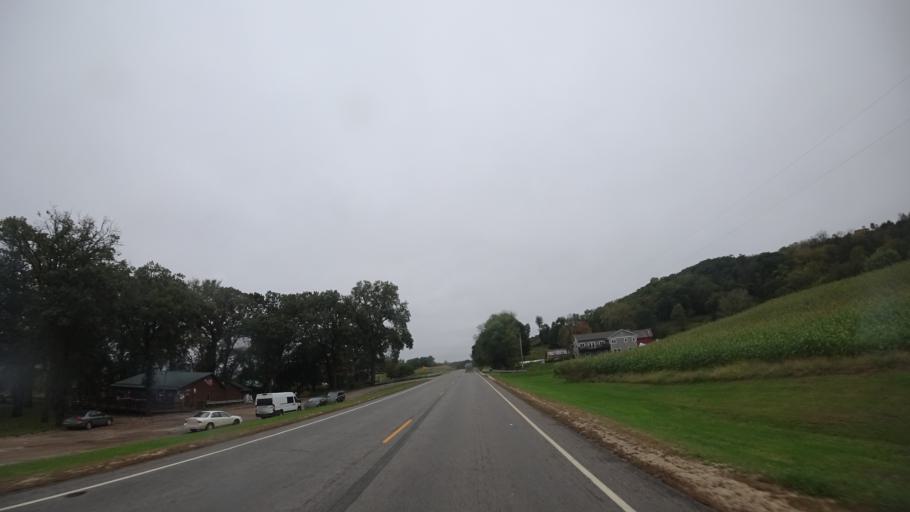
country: US
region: Wisconsin
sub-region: Crawford County
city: Prairie du Chien
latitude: 43.0532
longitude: -90.9741
